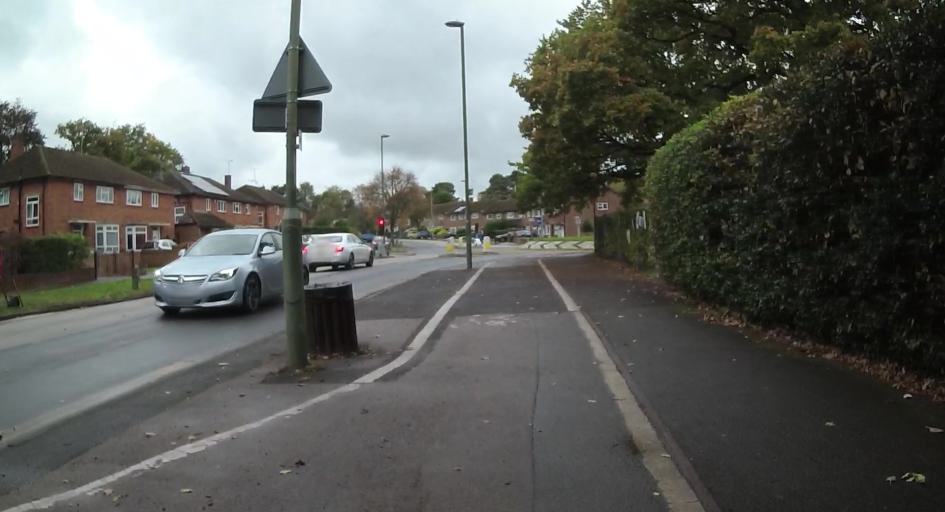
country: GB
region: England
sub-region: Surrey
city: West Byfleet
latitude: 51.3352
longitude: -0.5232
